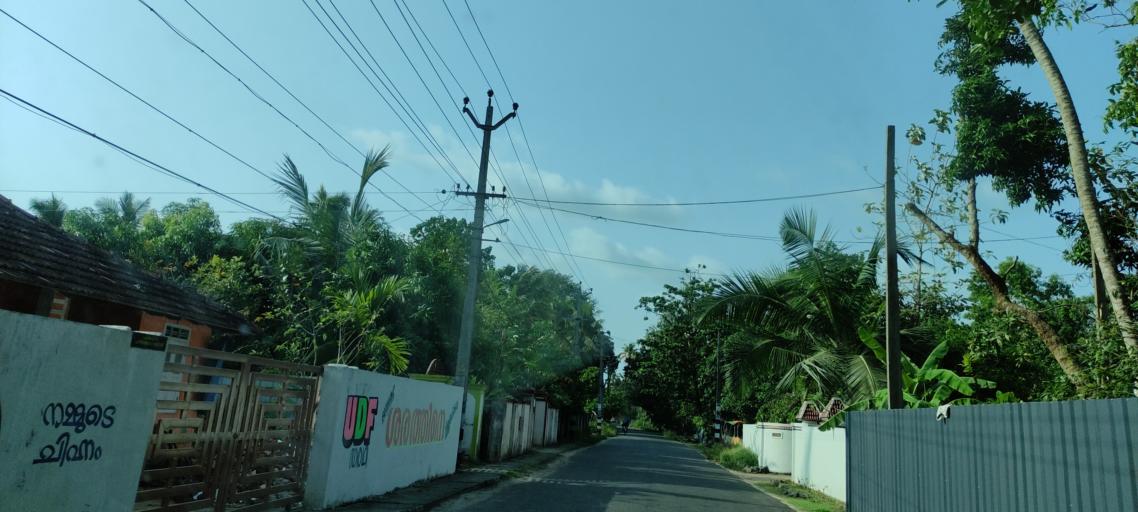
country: IN
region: Kerala
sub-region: Alappuzha
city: Vayalar
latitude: 9.6885
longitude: 76.2909
